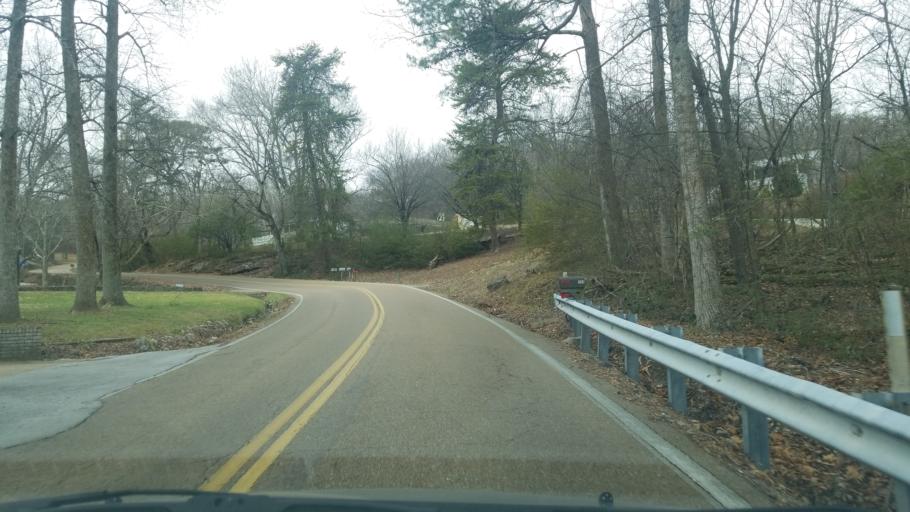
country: US
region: Tennessee
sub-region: Hamilton County
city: Soddy-Daisy
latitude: 35.2548
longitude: -85.1983
